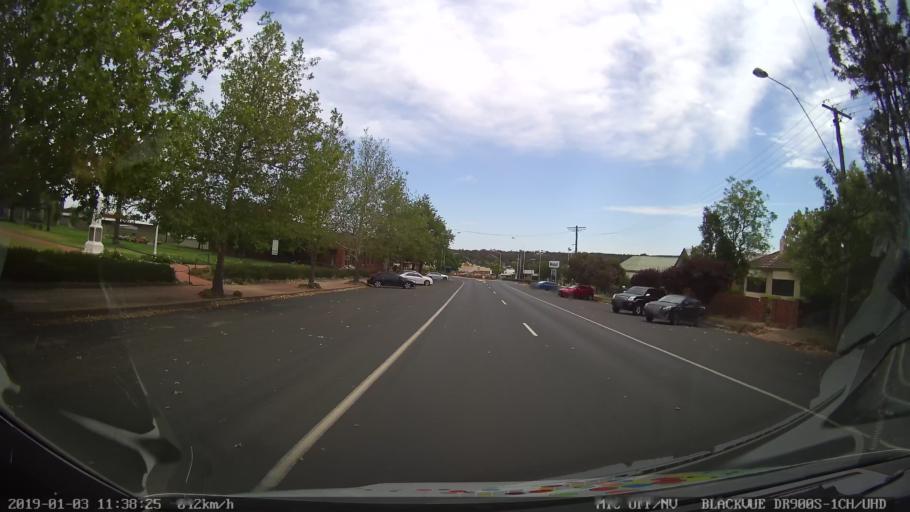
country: AU
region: New South Wales
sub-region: Weddin
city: Grenfell
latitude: -33.8963
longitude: 148.1625
